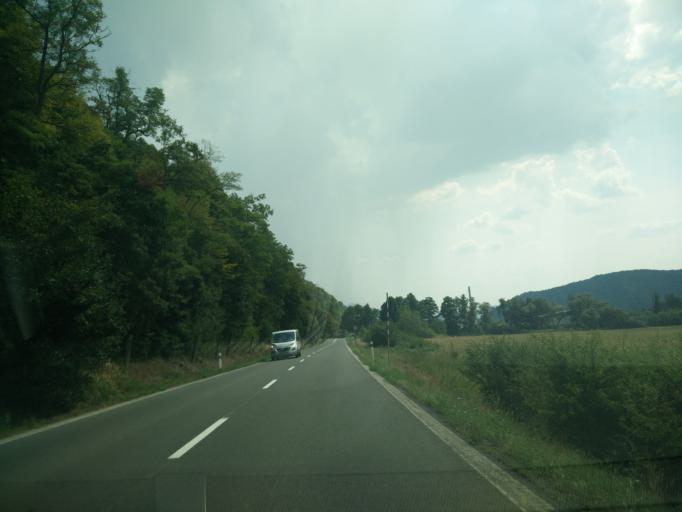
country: SK
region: Banskobystricky
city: Zarnovica
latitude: 48.5200
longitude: 18.7401
